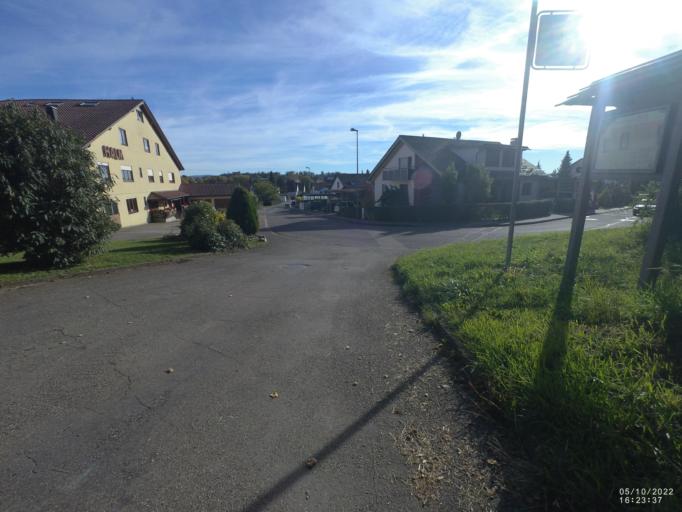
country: DE
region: Baden-Wuerttemberg
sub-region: Regierungsbezirk Stuttgart
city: Schlierbach
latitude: 48.6967
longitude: 9.5044
